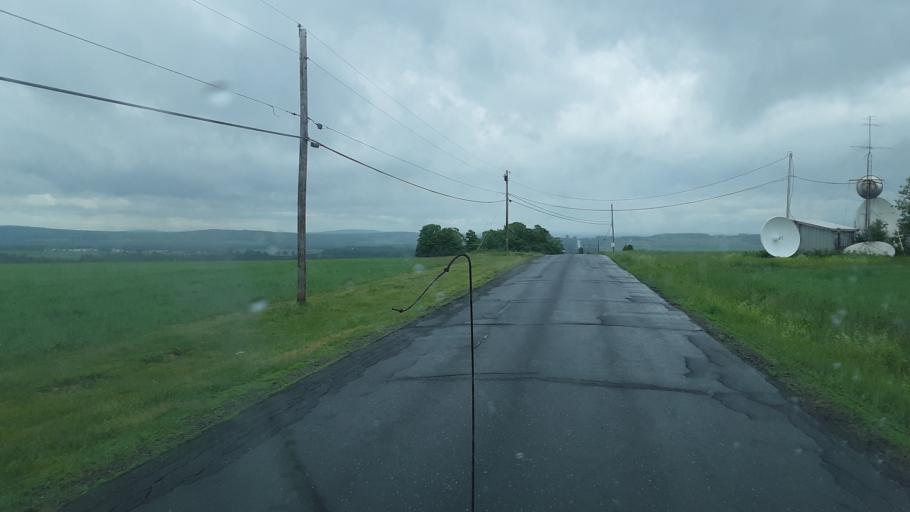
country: US
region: Maine
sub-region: Aroostook County
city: Presque Isle
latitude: 46.6818
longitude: -68.1852
